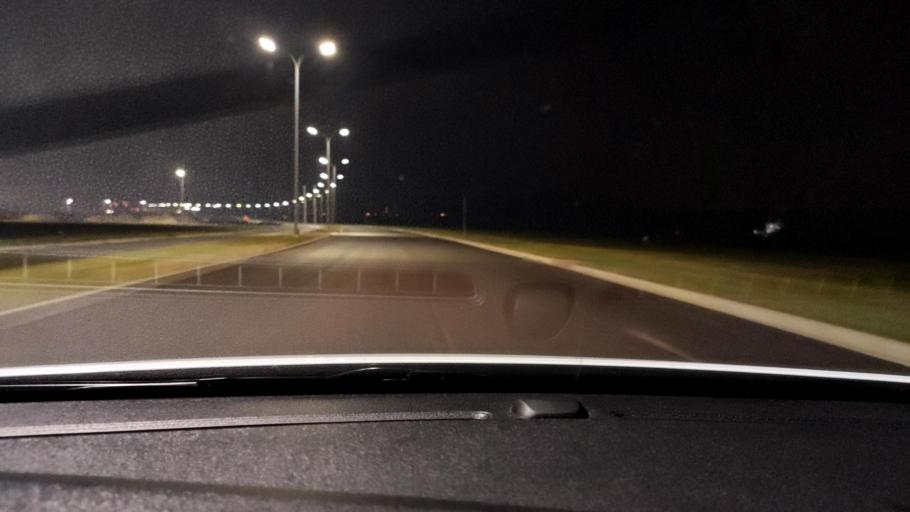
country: RU
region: Tatarstan
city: Sviyazhsk
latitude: 55.7420
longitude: 48.7478
